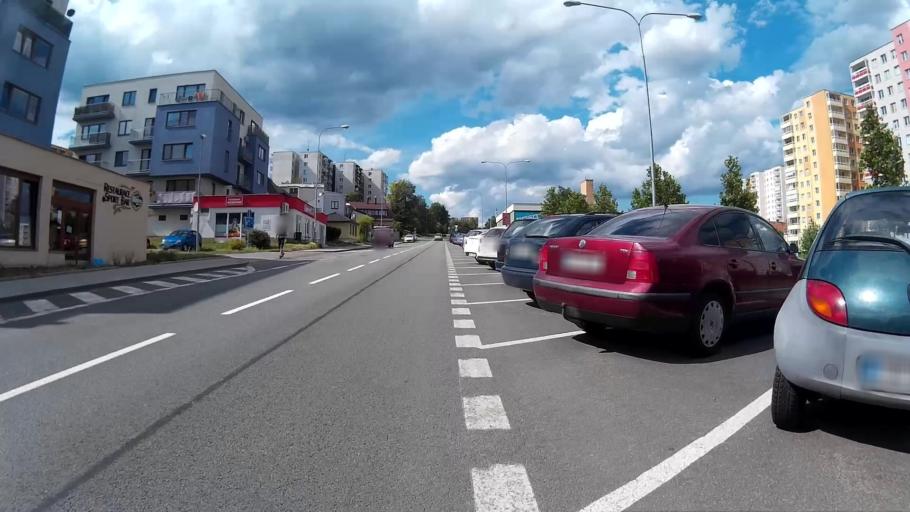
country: CZ
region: South Moravian
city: Moravany
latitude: 49.1671
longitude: 16.5755
